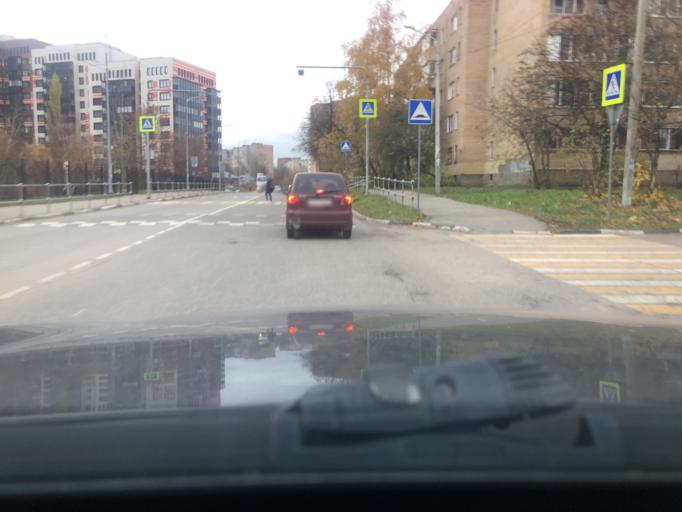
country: RU
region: Moskovskaya
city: Sergiyev Posad
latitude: 56.3226
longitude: 38.1321
